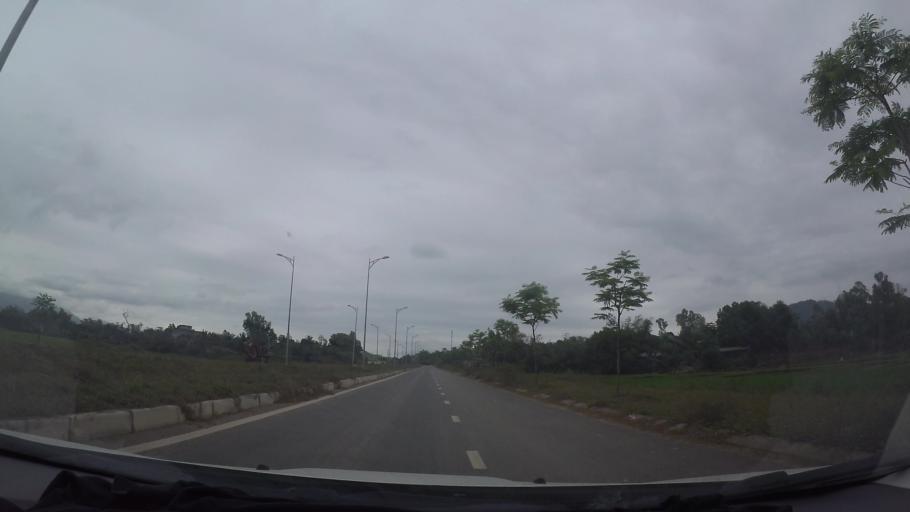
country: VN
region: Da Nang
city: Lien Chieu
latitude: 16.0768
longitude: 108.0933
